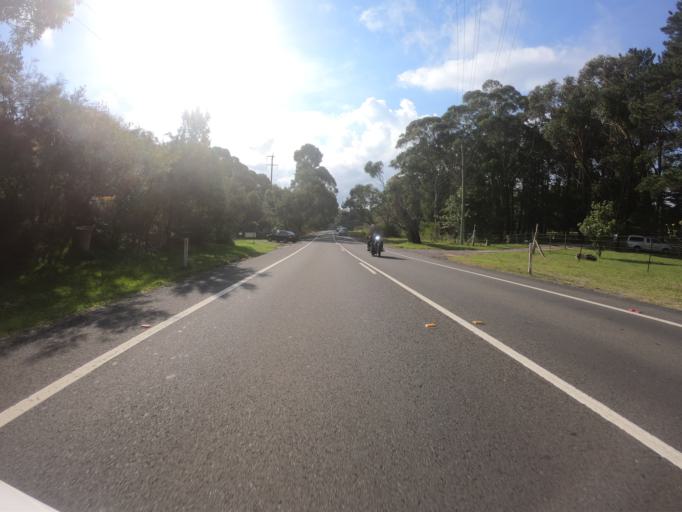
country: AU
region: New South Wales
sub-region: Wollongong
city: Helensburgh
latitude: -34.2162
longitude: 150.9777
